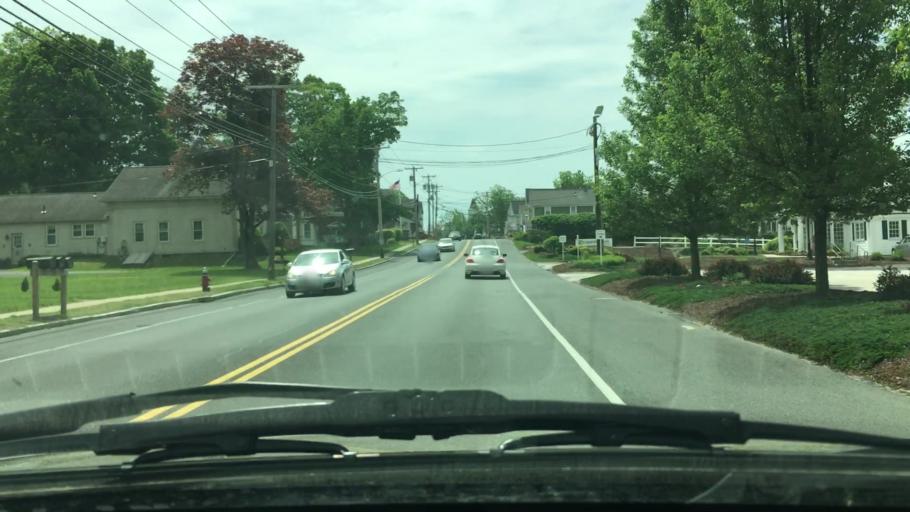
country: US
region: Massachusetts
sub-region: Hampshire County
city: Belchertown
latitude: 42.2816
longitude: -72.4046
